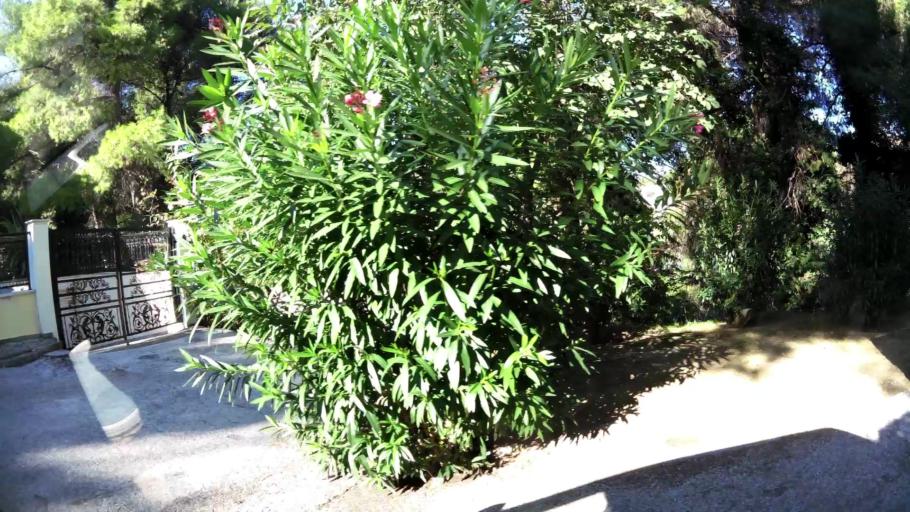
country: GR
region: Attica
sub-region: Nomarchia Athinas
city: Ekali
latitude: 38.1184
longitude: 23.8422
